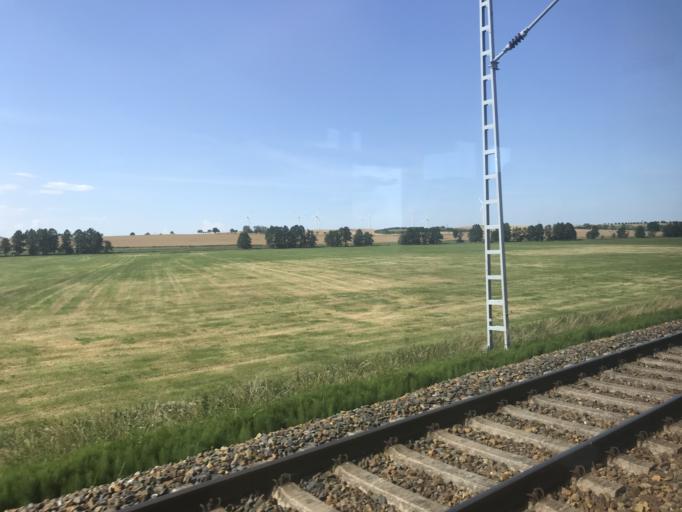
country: DE
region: Brandenburg
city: Passow
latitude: 53.1377
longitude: 14.0845
